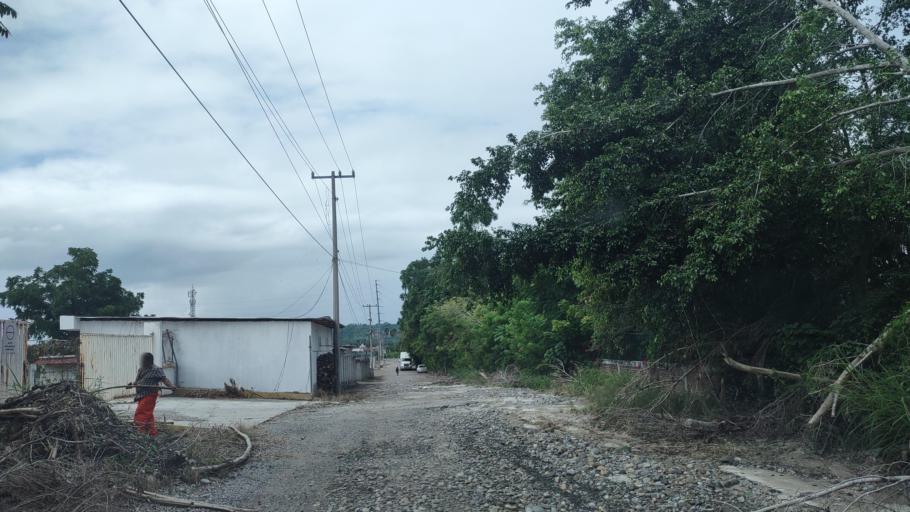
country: MX
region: Veracruz
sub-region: Papantla
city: Residencial Tajin
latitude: 20.5932
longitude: -97.4187
